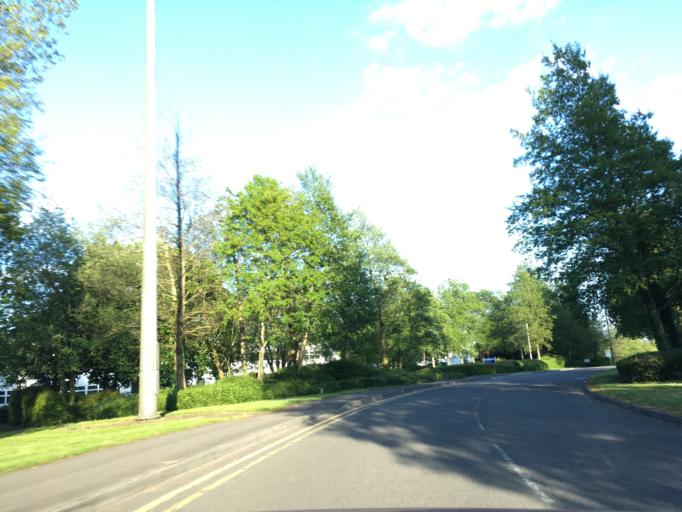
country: GB
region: Wales
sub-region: Newport
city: Marshfield
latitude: 51.5289
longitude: -3.0824
